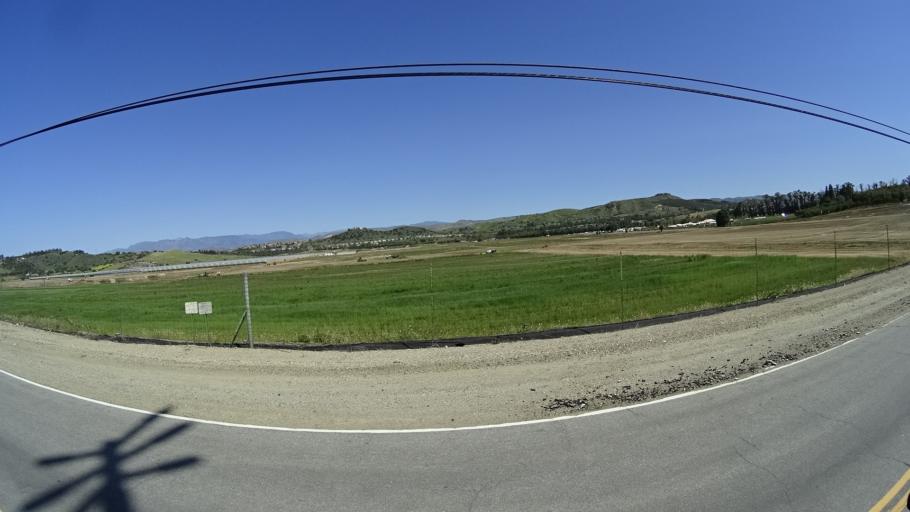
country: US
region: California
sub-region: Ventura County
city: Moorpark
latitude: 34.2498
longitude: -118.8555
